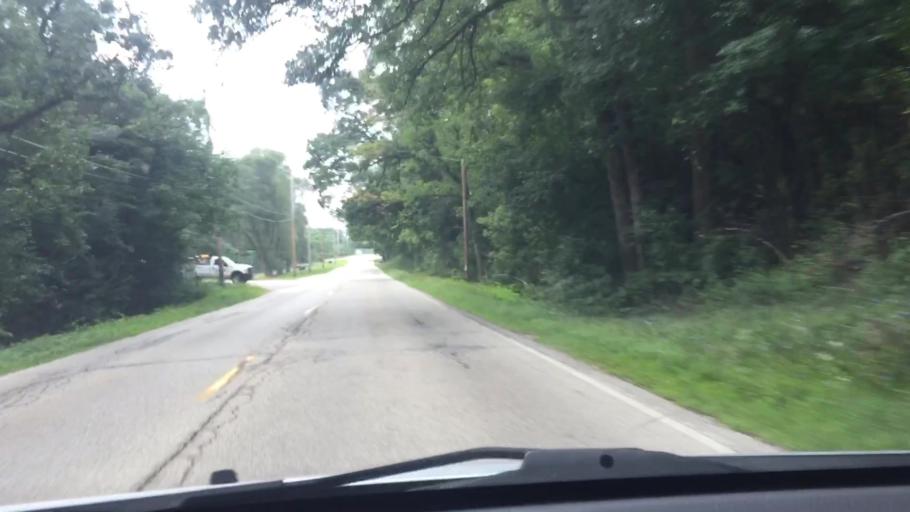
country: US
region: Wisconsin
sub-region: Waukesha County
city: Dousman
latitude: 43.0404
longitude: -88.4425
